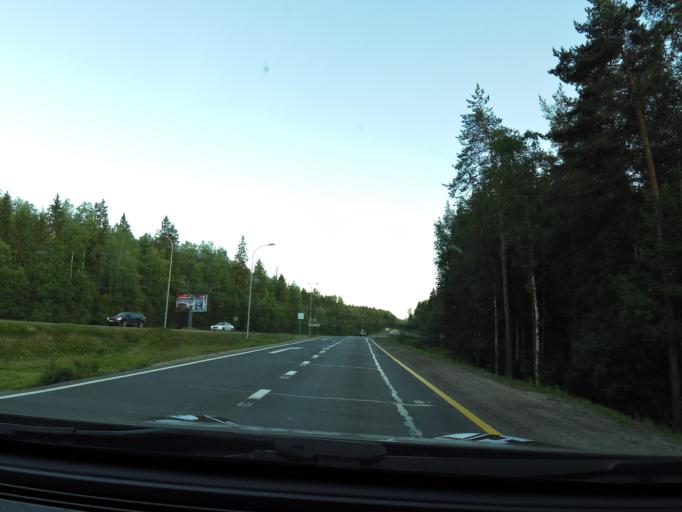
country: RU
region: Vologda
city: Gryazovets
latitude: 58.8809
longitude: 40.1925
